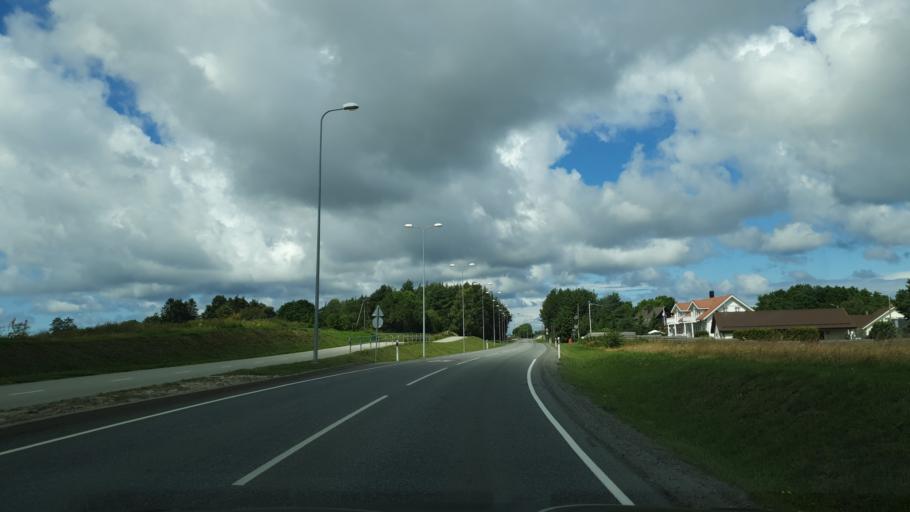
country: EE
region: Harju
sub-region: Viimsi vald
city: Viimsi
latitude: 59.4941
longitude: 24.8766
